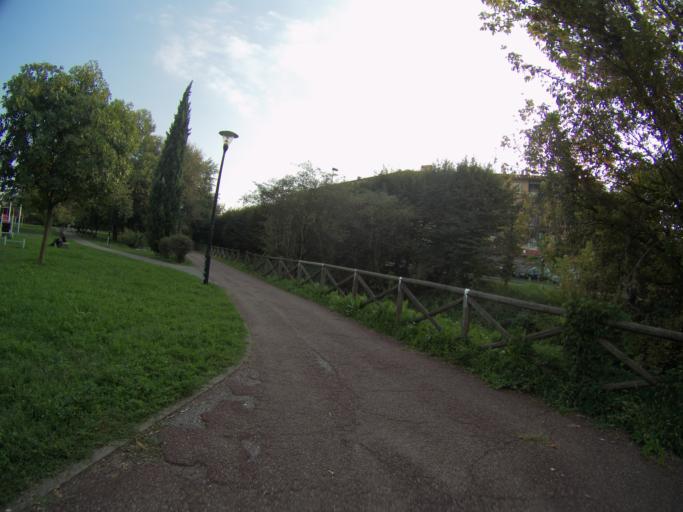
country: IT
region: Lombardy
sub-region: Citta metropolitana di Milano
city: Vignate
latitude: 45.4923
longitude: 9.3751
